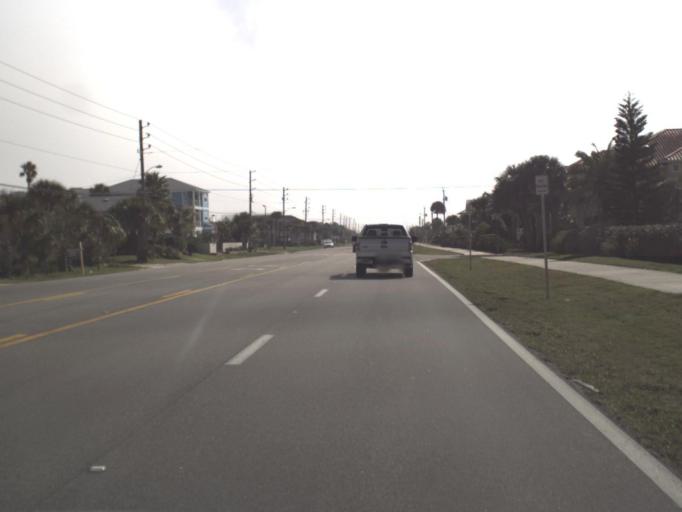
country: US
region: Florida
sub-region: Volusia County
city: Edgewater
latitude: 29.0164
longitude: -80.8839
